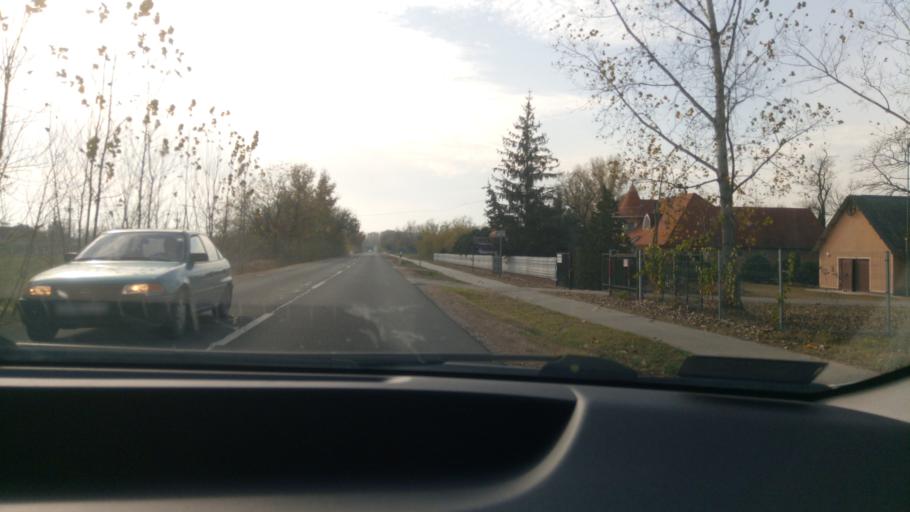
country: HU
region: Bacs-Kiskun
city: Jaszszentlaszlo
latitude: 46.5498
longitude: 19.7463
